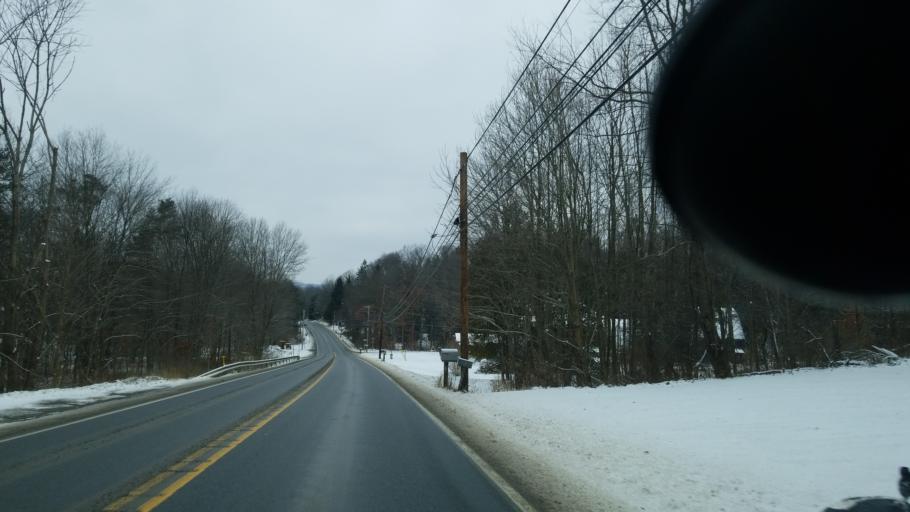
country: US
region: Pennsylvania
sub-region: Jefferson County
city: Albion
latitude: 40.9372
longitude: -78.9216
